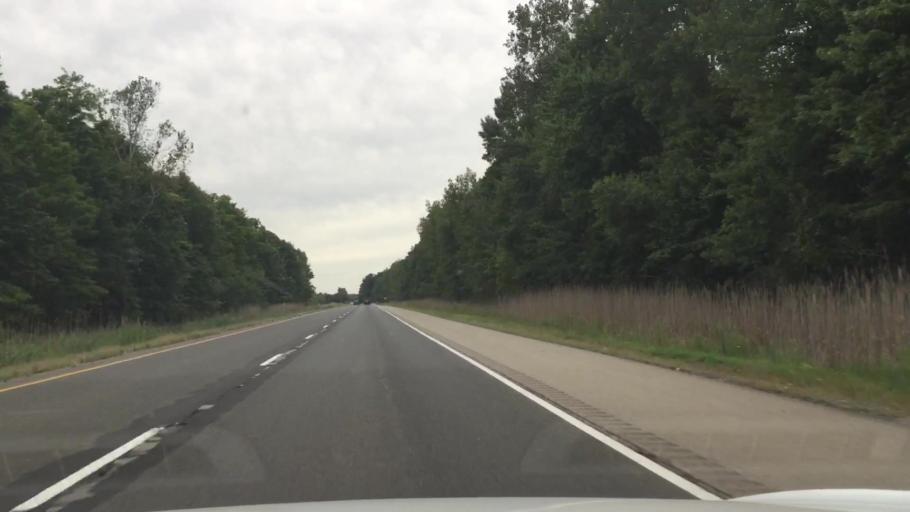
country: CA
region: Ontario
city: Lambton Shores
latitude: 42.9922
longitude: -81.9266
